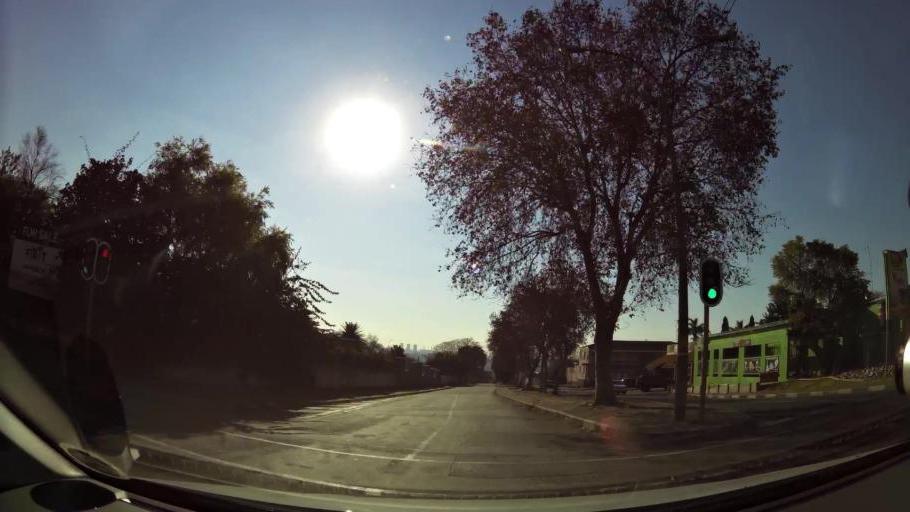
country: ZA
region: Gauteng
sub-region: City of Johannesburg Metropolitan Municipality
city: Modderfontein
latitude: -26.1403
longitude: 28.1542
